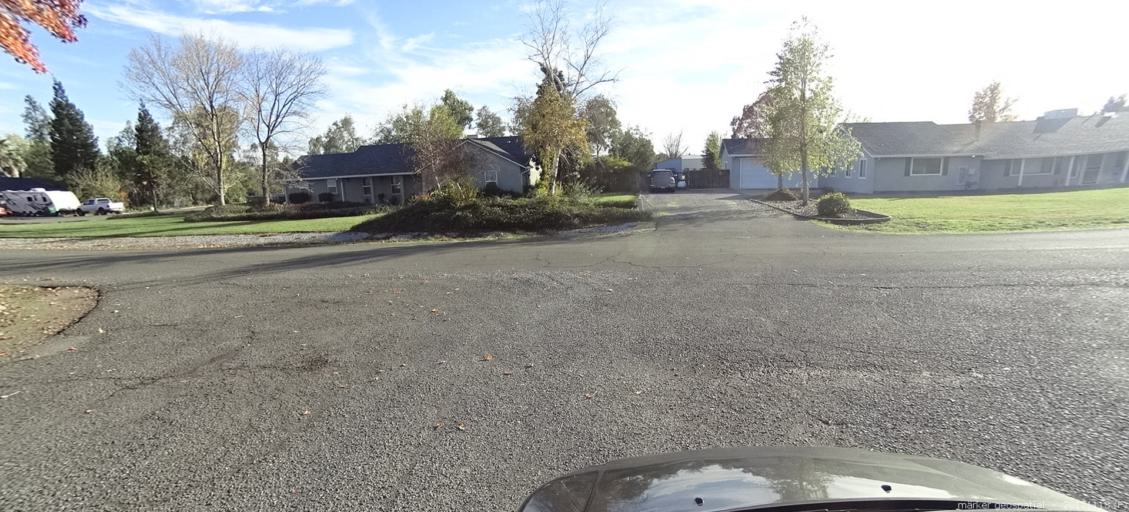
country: US
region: California
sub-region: Shasta County
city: Cottonwood
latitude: 40.3813
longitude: -122.3363
